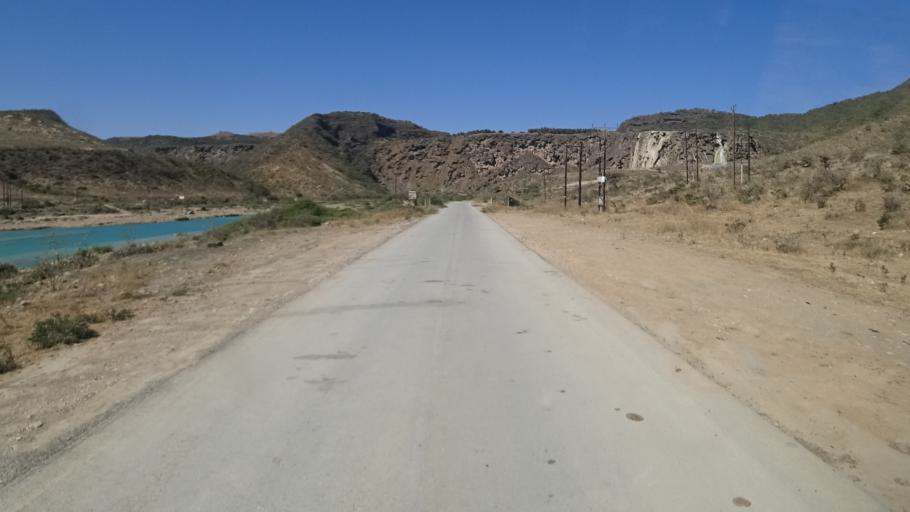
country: OM
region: Zufar
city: Salalah
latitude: 17.0692
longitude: 54.4317
